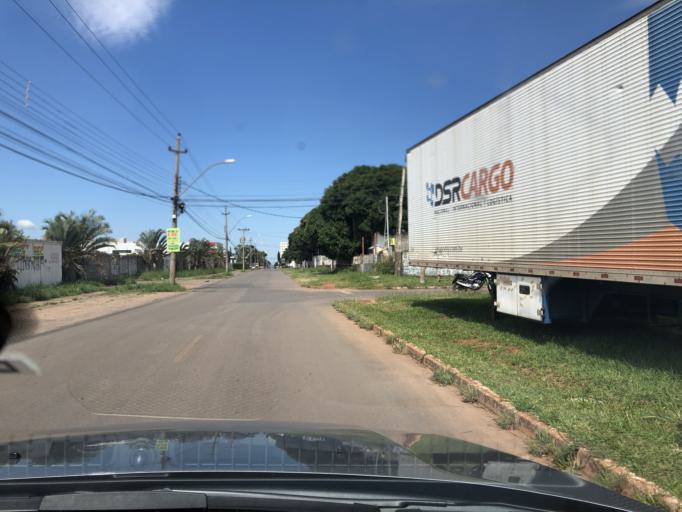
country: BR
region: Federal District
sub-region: Brasilia
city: Brasilia
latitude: -16.0051
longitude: -48.0547
